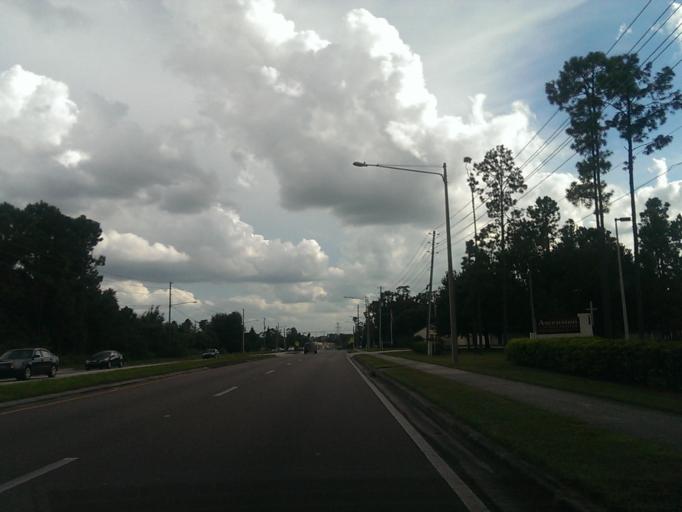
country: US
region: Florida
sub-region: Orange County
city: Bay Hill
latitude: 28.4898
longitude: -81.5086
